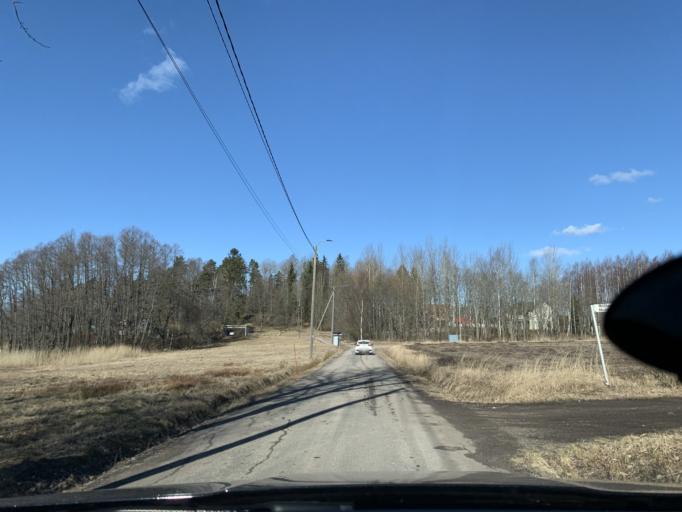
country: FI
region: Uusimaa
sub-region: Helsinki
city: Espoo
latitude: 60.1730
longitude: 24.5822
